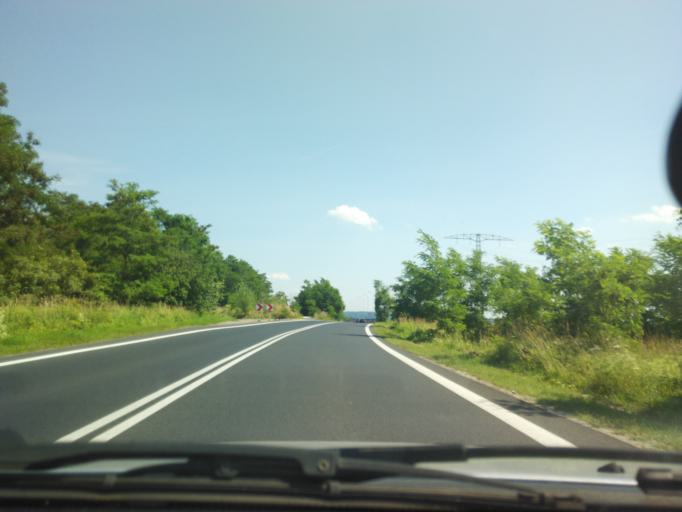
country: PL
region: West Pomeranian Voivodeship
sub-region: Szczecin
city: Szczecin
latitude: 53.3842
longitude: 14.5314
